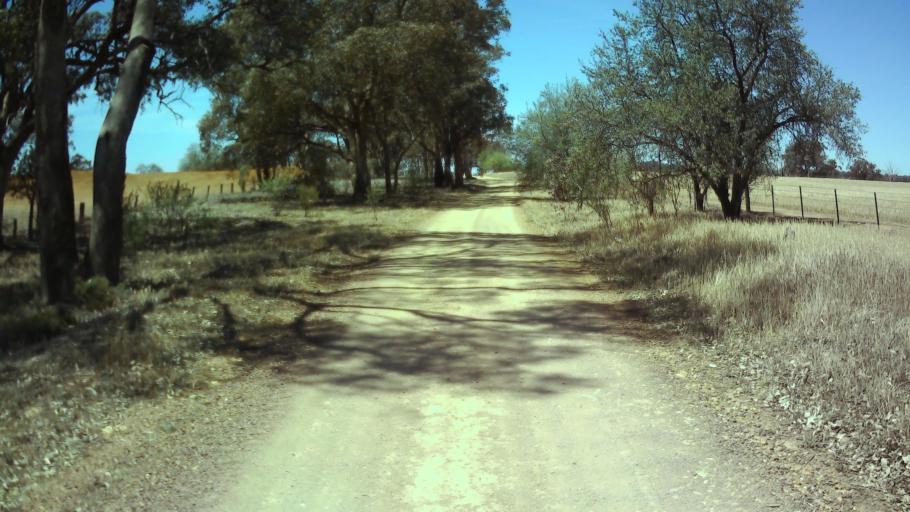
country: AU
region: New South Wales
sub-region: Weddin
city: Grenfell
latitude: -33.9284
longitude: 148.1760
